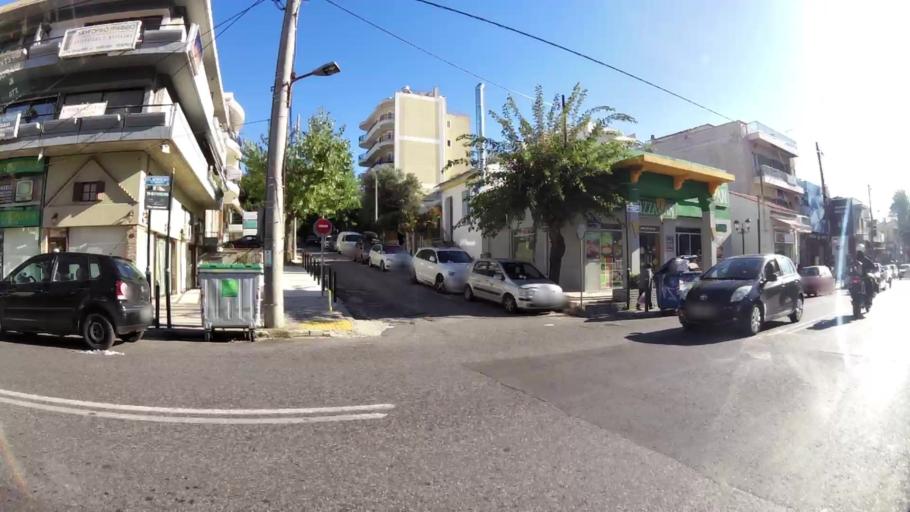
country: GR
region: Attica
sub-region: Nomarchia Athinas
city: Nea Erythraia
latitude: 38.0902
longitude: 23.8199
